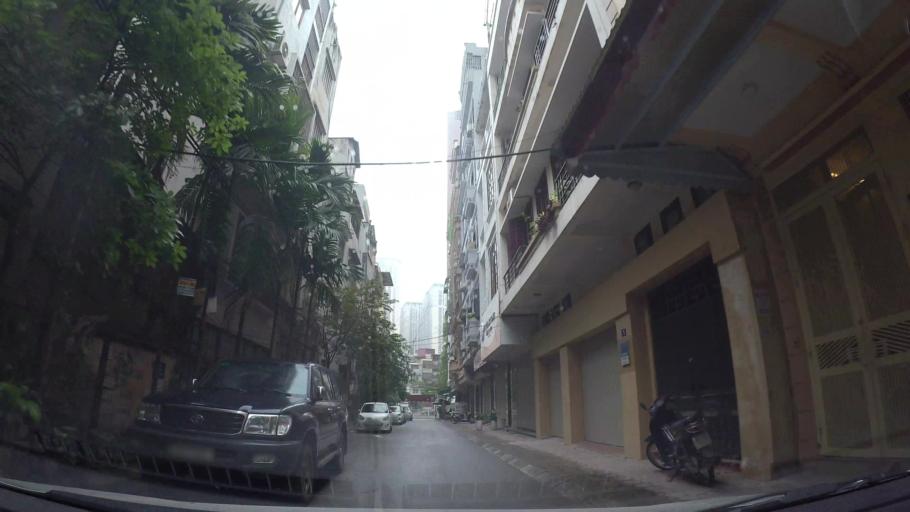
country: VN
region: Ha Noi
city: Cau Giay
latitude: 21.0186
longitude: 105.7906
